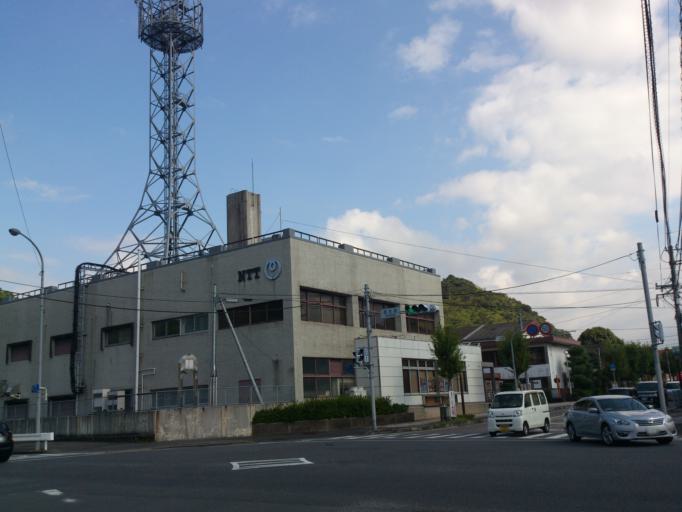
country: JP
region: Saga Prefecture
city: Imaricho-ko
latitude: 33.1813
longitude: 129.8857
